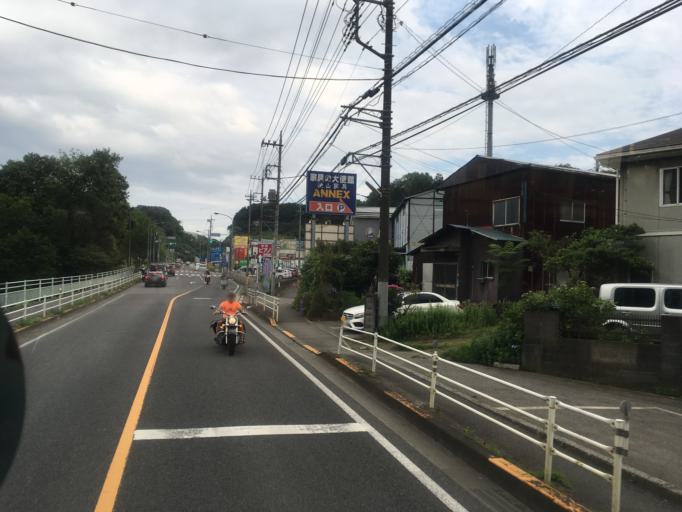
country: JP
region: Tokyo
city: Hachioji
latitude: 35.6250
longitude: 139.3385
